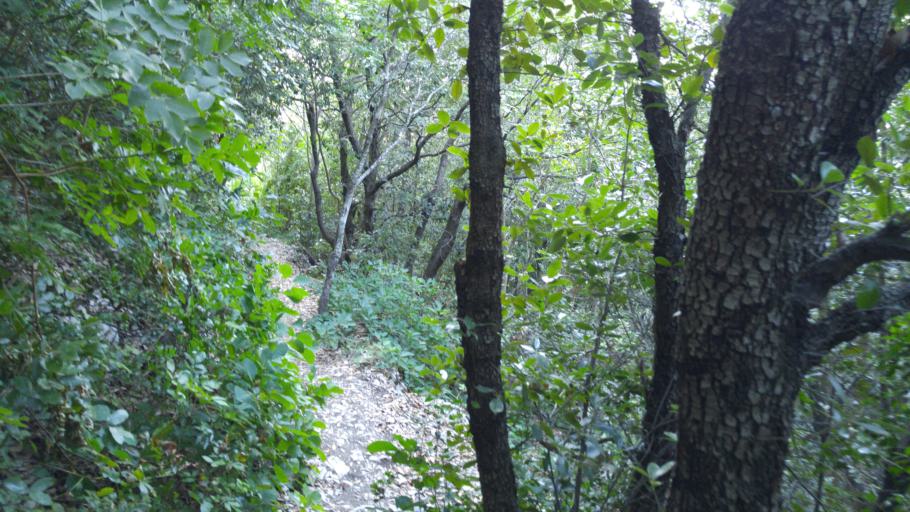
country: IT
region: The Marches
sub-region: Provincia di Pesaro e Urbino
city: Canavaccio
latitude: 43.6553
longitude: 12.7321
